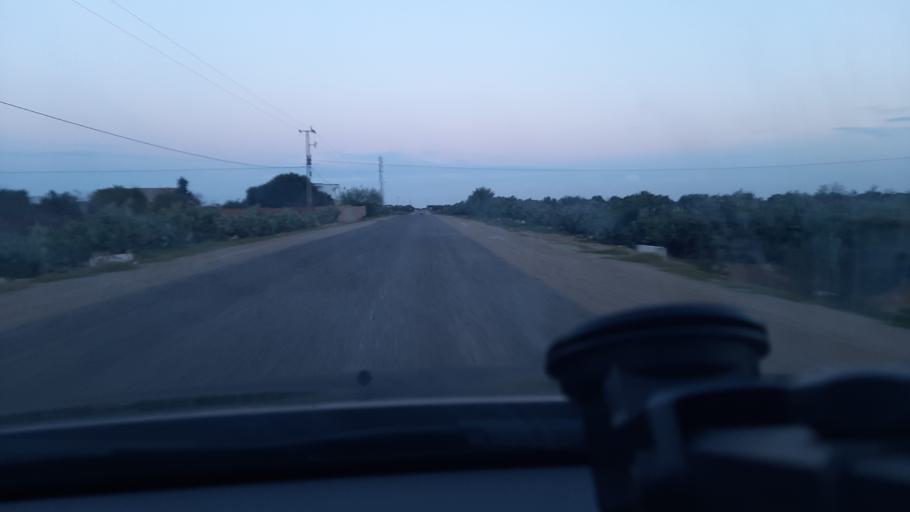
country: TN
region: Al Mahdiyah
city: Shurban
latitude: 35.0177
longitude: 10.4544
